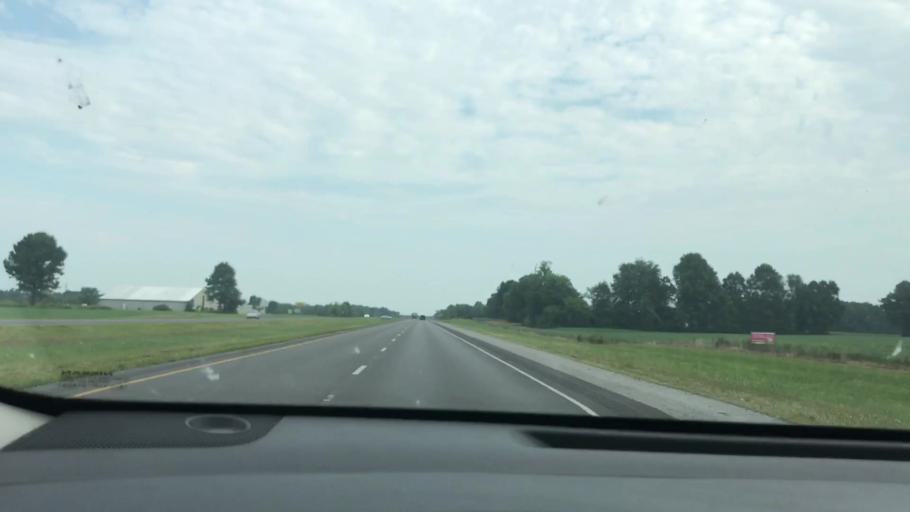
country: US
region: Kentucky
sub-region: Calloway County
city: Murray
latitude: 36.6882
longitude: -88.3029
